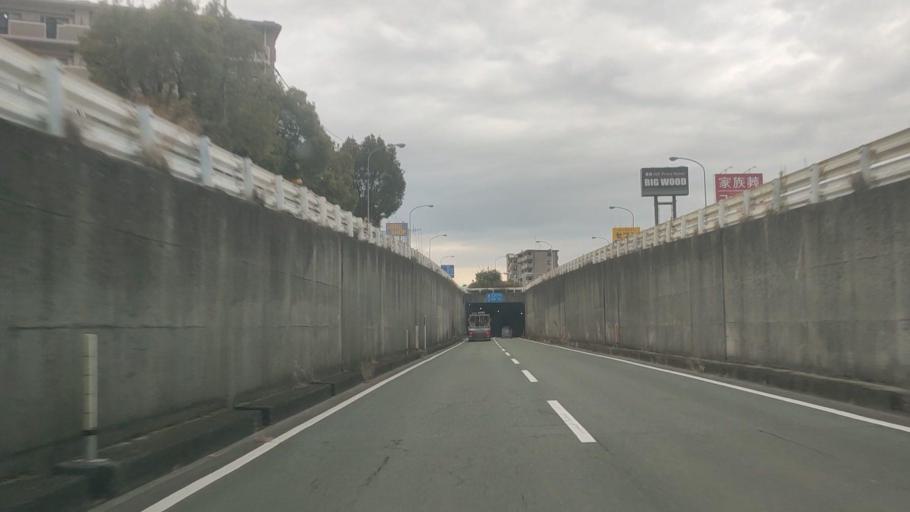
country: JP
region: Kumamoto
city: Ozu
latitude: 32.8520
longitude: 130.7831
